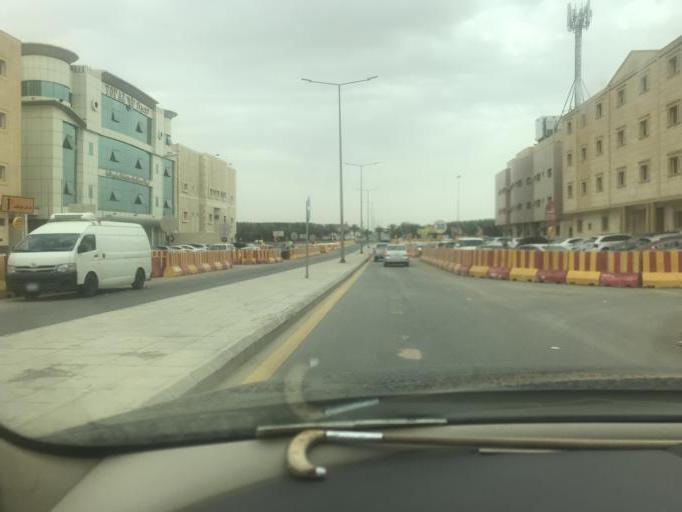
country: SA
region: Ar Riyad
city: Riyadh
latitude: 24.7902
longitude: 46.7114
